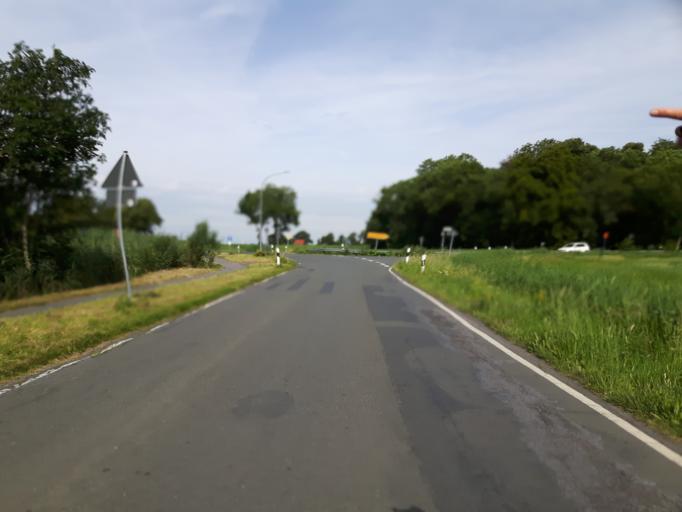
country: DE
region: Lower Saxony
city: Elsfleth
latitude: 53.2554
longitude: 8.4708
